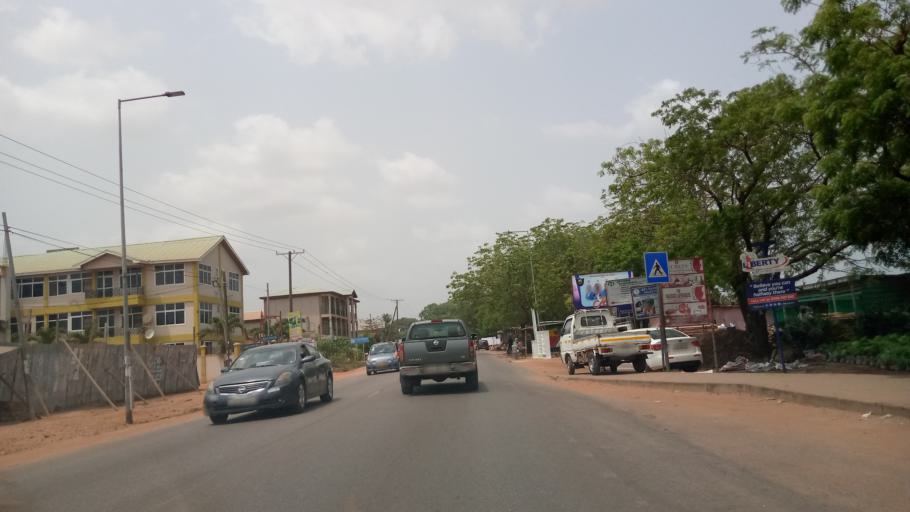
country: GH
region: Greater Accra
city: Dome
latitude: 5.6676
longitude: -0.2157
